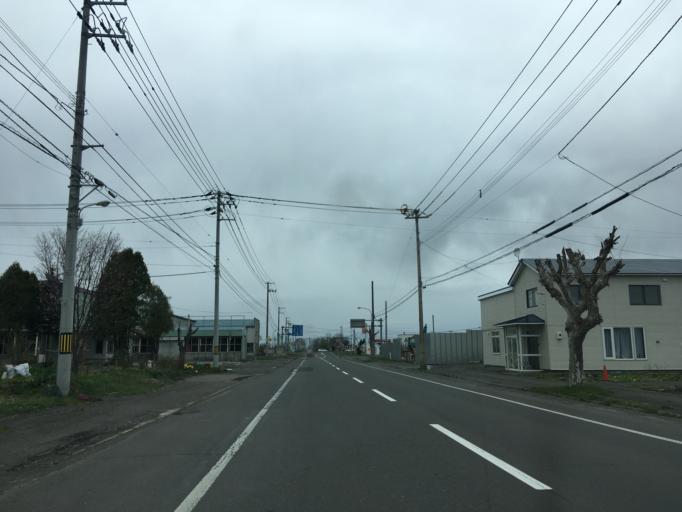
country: JP
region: Hokkaido
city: Chitose
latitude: 42.9479
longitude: 141.8030
